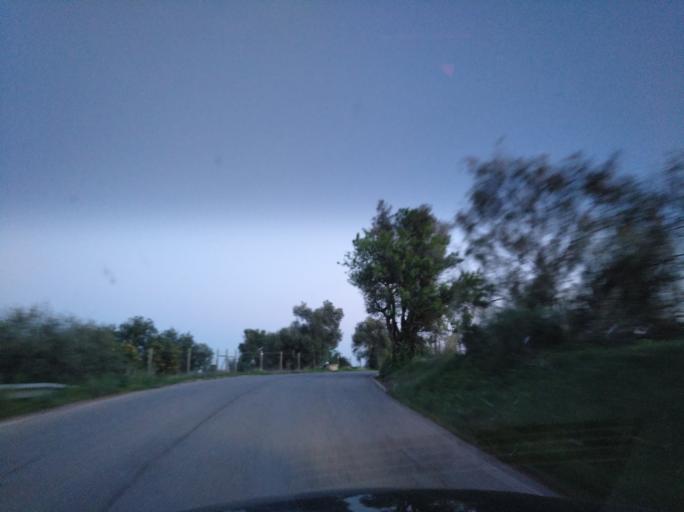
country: PT
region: Faro
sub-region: Vila Real de Santo Antonio
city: Monte Gordo
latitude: 37.1941
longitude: -7.5147
